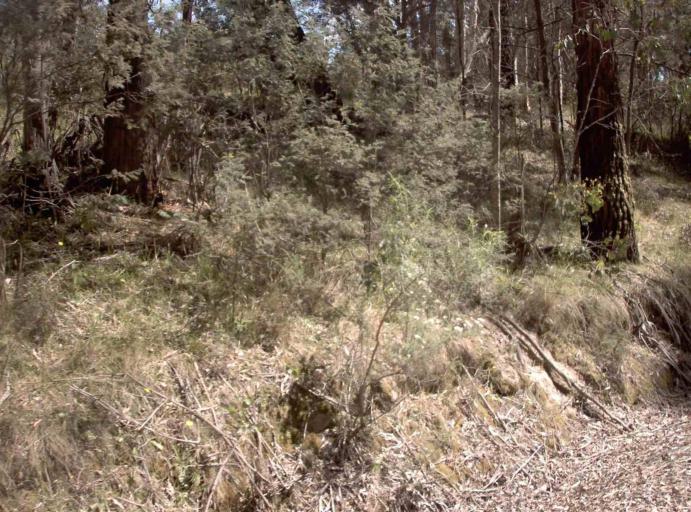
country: AU
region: New South Wales
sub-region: Bombala
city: Bombala
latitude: -37.0642
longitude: 148.7987
